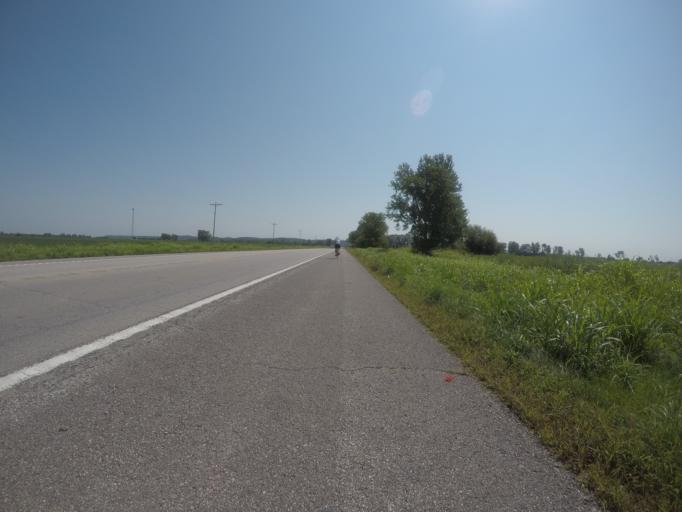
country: US
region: Kansas
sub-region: Atchison County
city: Atchison
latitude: 39.5568
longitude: -95.0844
